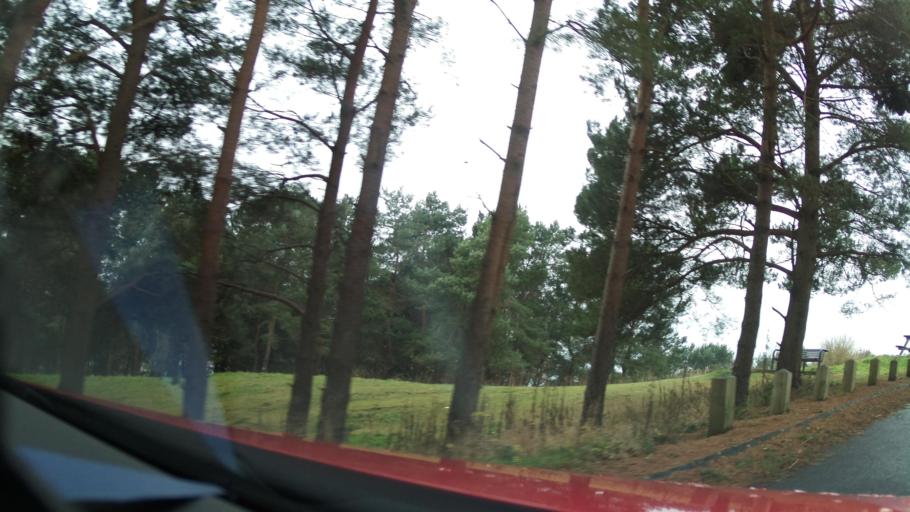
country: GB
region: Scotland
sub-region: Dundee City
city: Dundee
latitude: 56.4693
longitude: -2.9899
